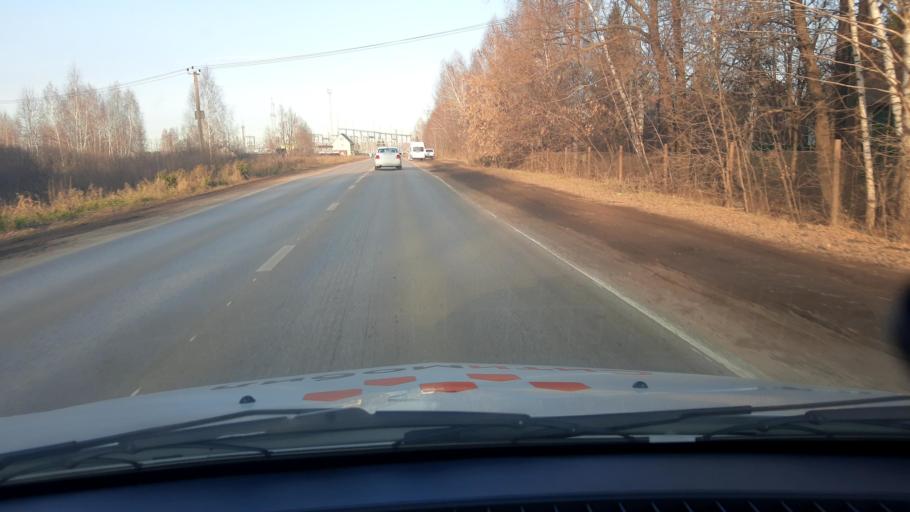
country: RU
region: Bashkortostan
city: Ufa
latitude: 54.6677
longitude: 56.0789
